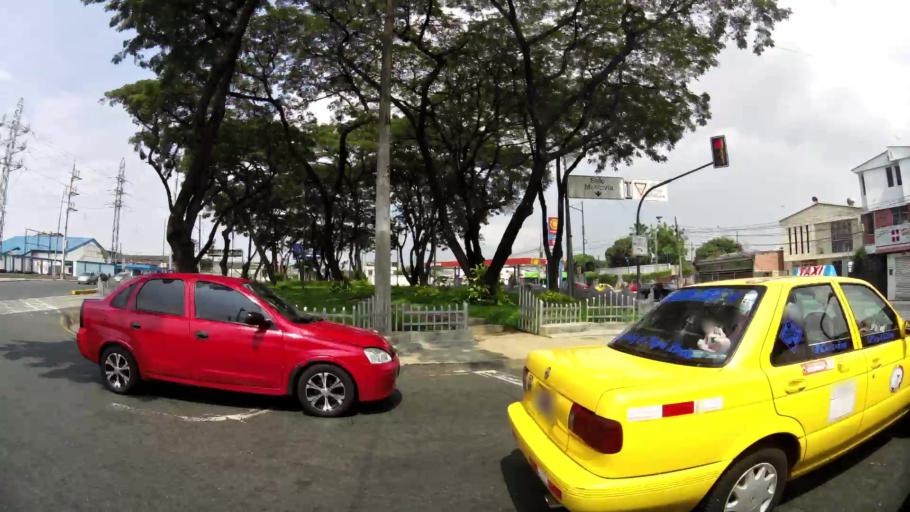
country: EC
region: Guayas
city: Guayaquil
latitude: -2.2306
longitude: -79.8903
